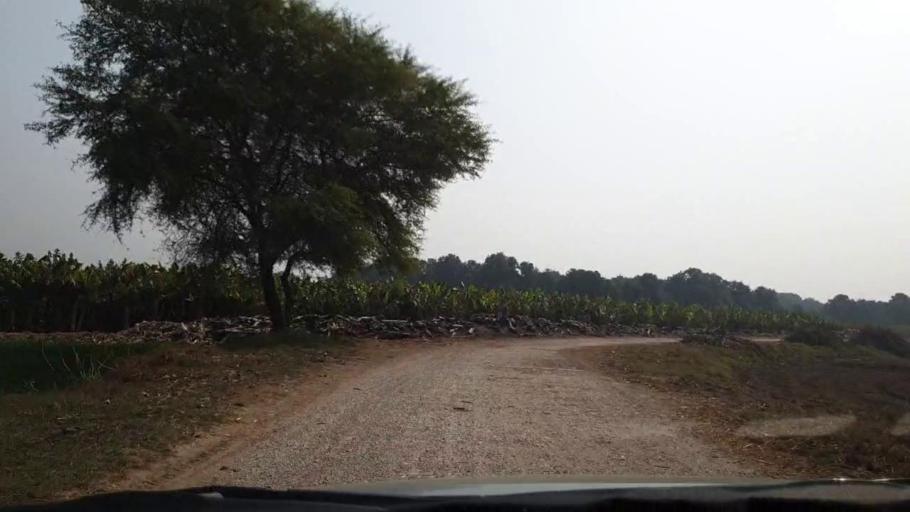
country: PK
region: Sindh
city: Matiari
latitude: 25.6386
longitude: 68.5178
